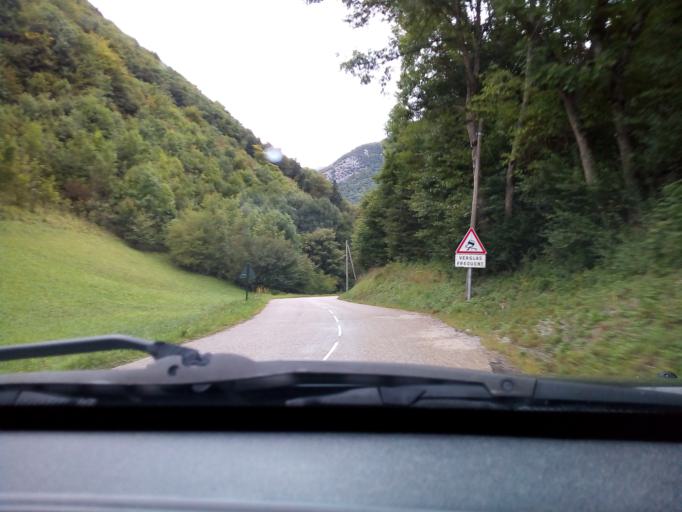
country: FR
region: Rhone-Alpes
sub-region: Departement de l'Isere
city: Corenc
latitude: 45.2363
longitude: 5.7511
